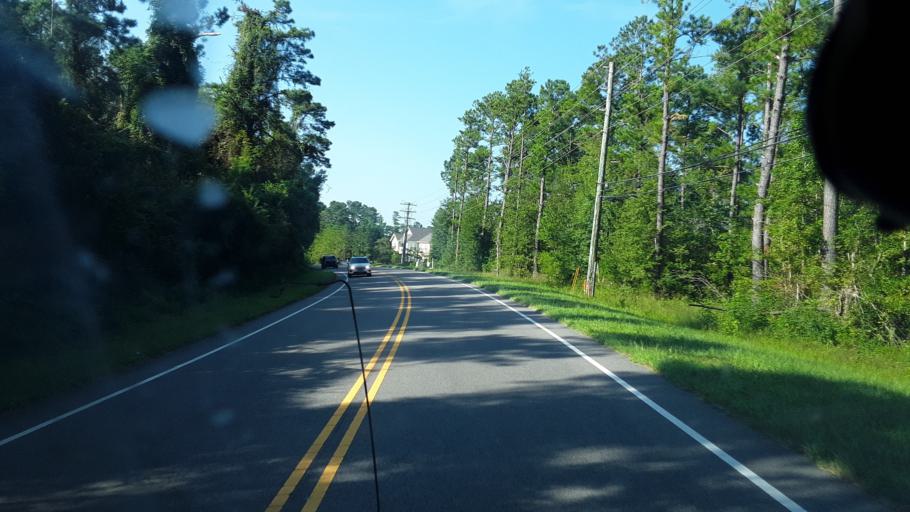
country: US
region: North Carolina
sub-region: Brunswick County
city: Belville
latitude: 34.1947
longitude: -77.9855
